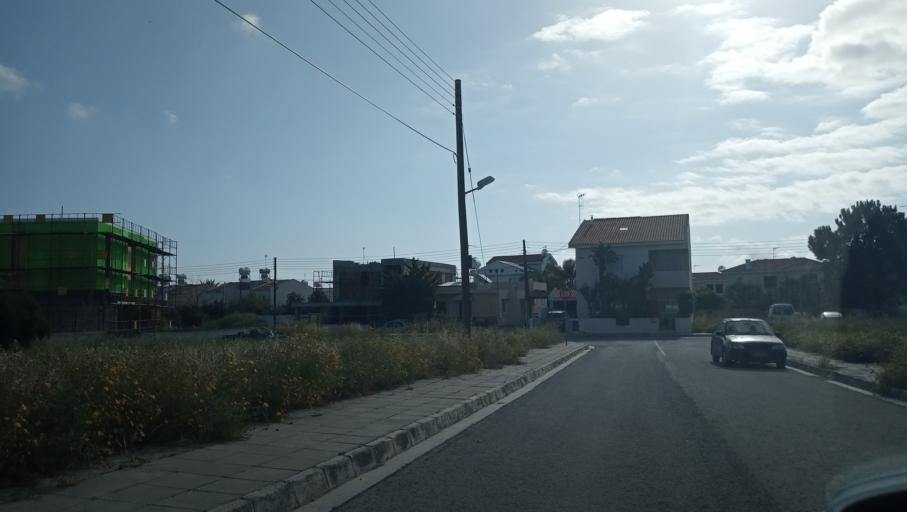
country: CY
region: Lefkosia
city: Tseri
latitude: 35.1152
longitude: 33.3356
